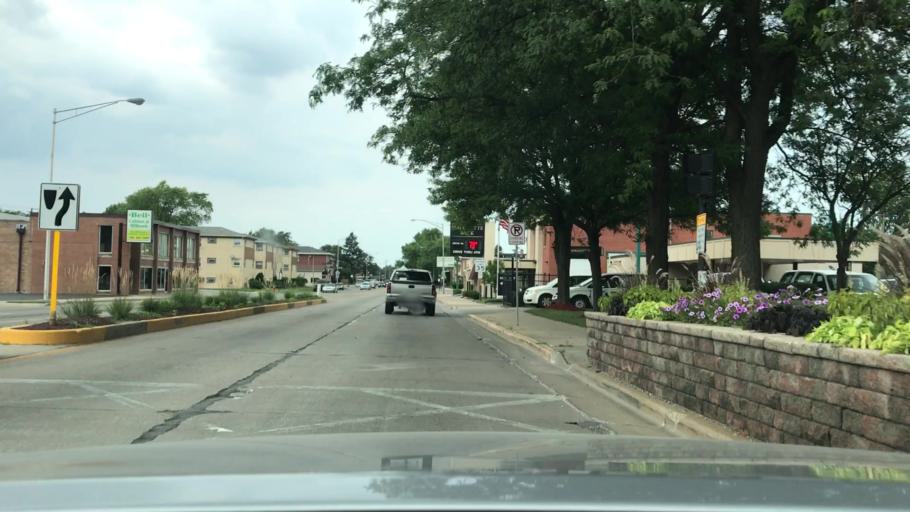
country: US
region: Illinois
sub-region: Cook County
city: Evergreen Park
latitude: 41.7226
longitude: -87.7018
